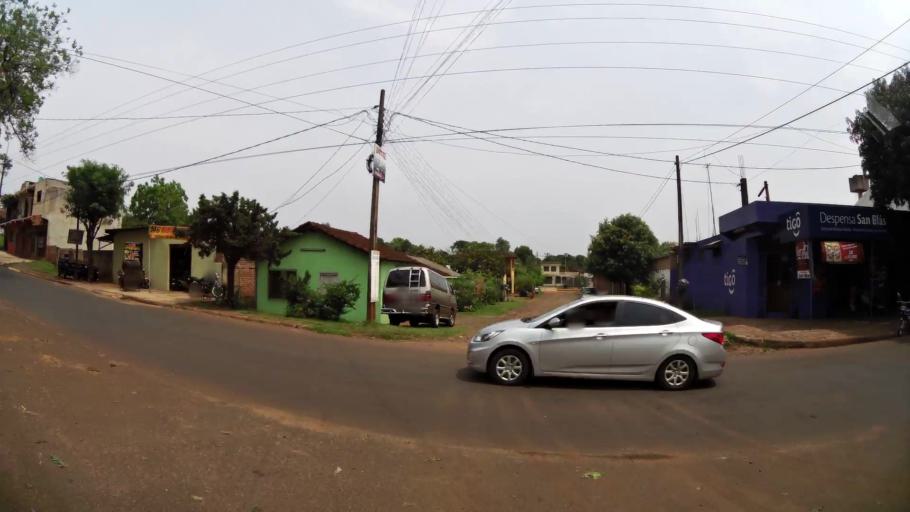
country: PY
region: Alto Parana
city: Presidente Franco
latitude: -25.5514
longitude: -54.6276
